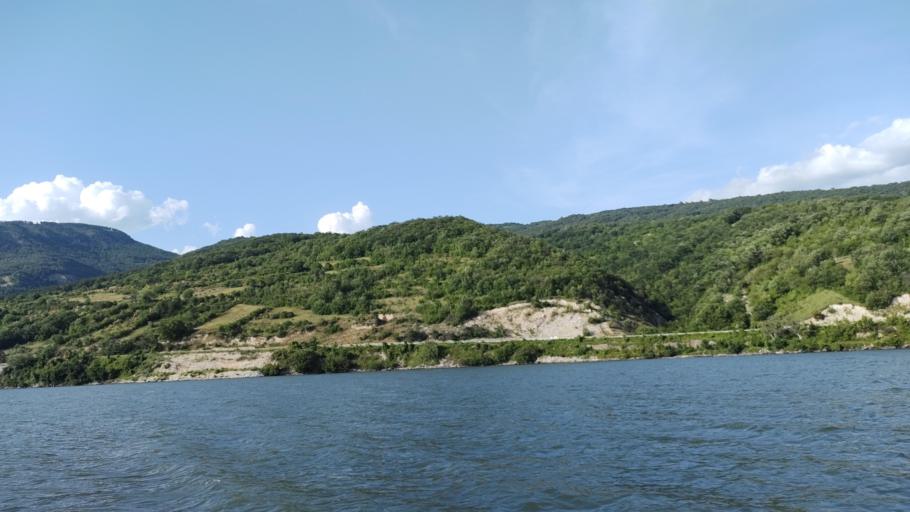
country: RO
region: Mehedinti
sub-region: Comuna Svinita
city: Svinita
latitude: 44.4881
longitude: 22.1108
